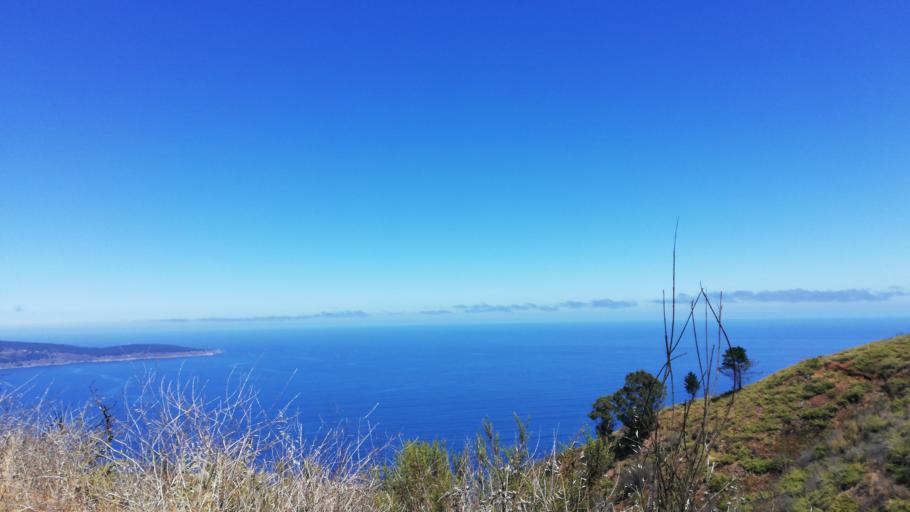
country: CL
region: Valparaiso
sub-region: Provincia de Valparaiso
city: Valparaiso
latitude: -33.0731
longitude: -71.6576
